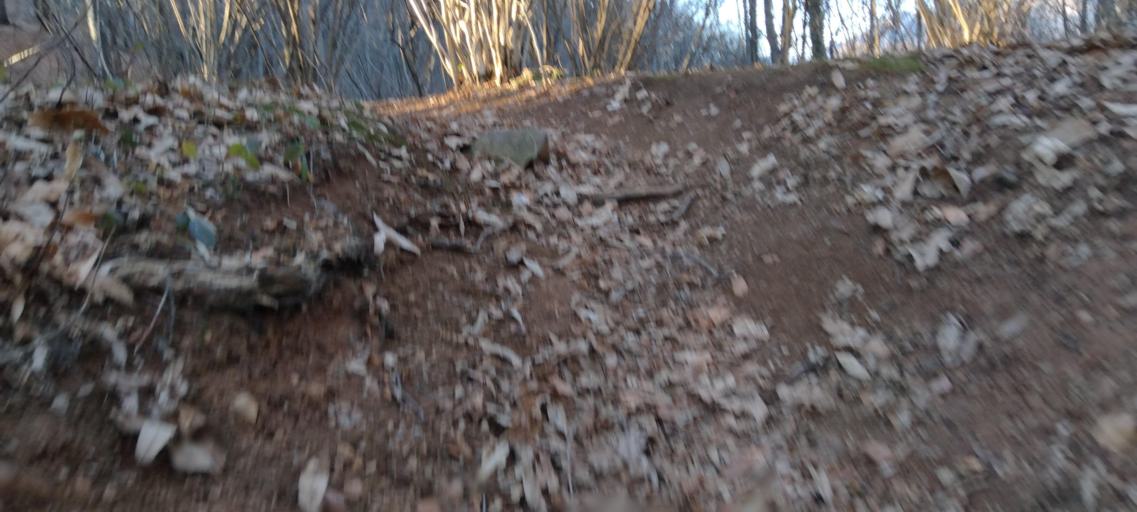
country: IT
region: Veneto
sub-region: Provincia di Vicenza
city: Valdagno
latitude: 45.6720
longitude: 11.3252
